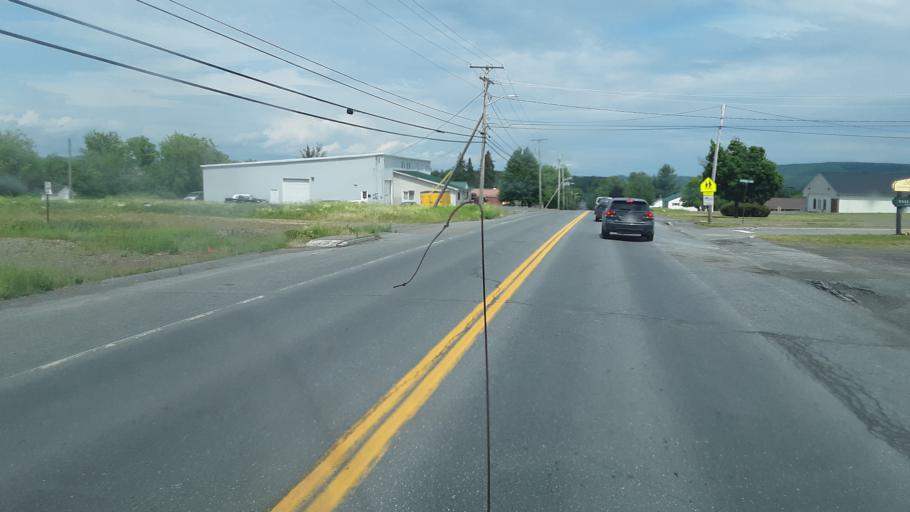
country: US
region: Maine
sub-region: Aroostook County
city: Fort Fairfield
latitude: 46.7672
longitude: -67.8457
